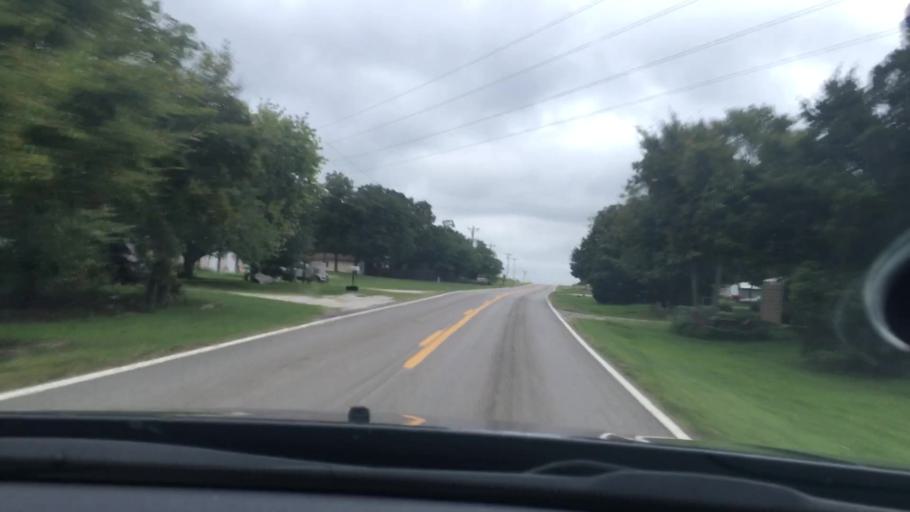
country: US
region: Oklahoma
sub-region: Sequoyah County
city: Vian
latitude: 35.6025
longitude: -95.0155
